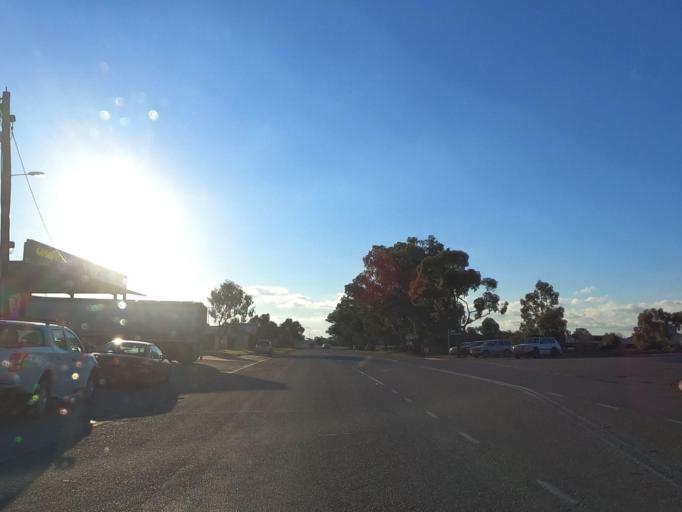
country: AU
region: Victoria
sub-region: Swan Hill
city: Swan Hill
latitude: -35.3304
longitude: 143.5563
